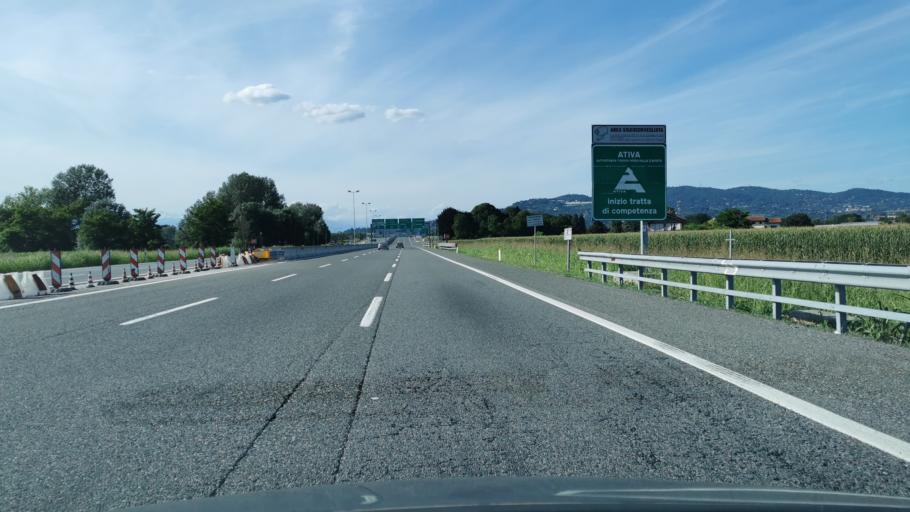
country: IT
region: Piedmont
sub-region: Provincia di Torino
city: La Loggia
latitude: 44.9640
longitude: 7.7044
